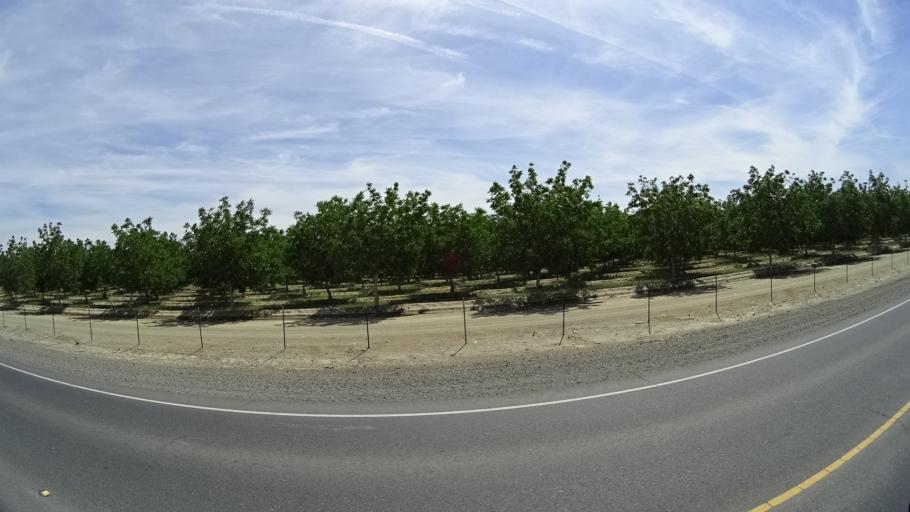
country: US
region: California
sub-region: Kings County
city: Hanford
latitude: 36.3370
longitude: -119.6010
